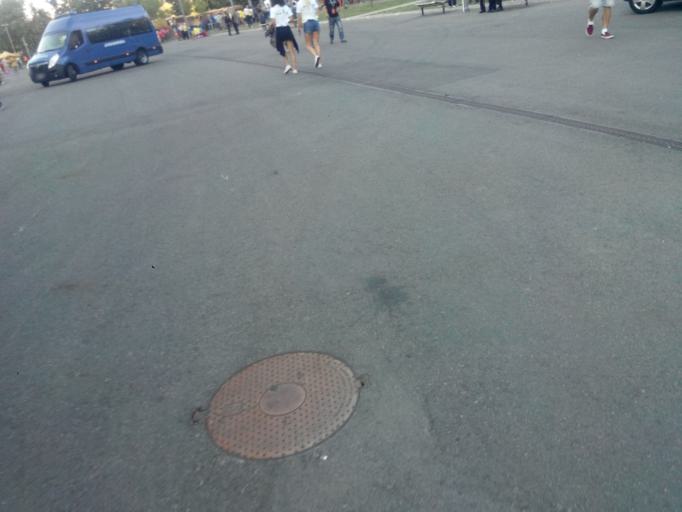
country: RO
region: Ilfov
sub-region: Comuna Fundeni-Dobroesti
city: Fundeni
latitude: 44.4367
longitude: 26.1544
